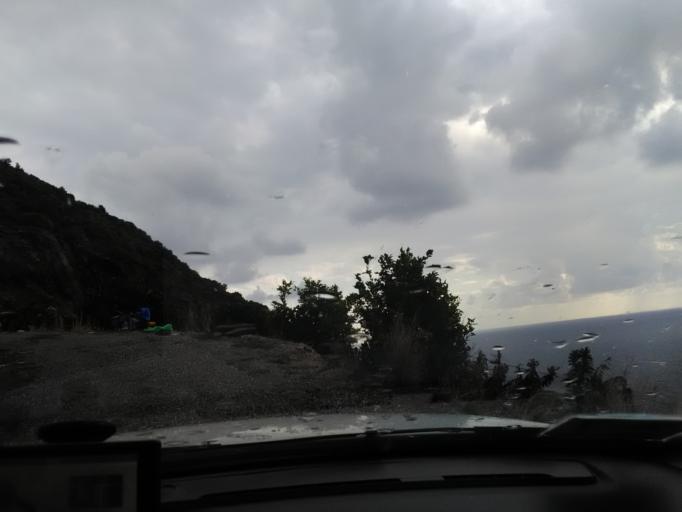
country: TR
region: Antalya
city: Gazipasa
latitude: 36.1567
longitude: 32.4189
